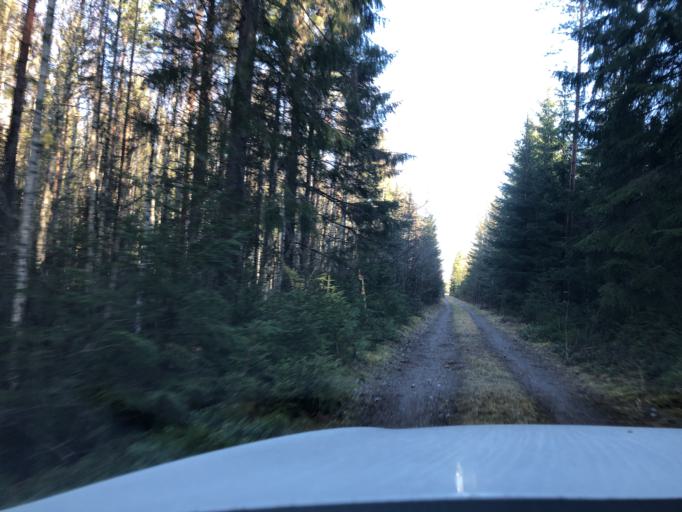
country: SE
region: Gaevleborg
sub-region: Gavle Kommun
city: Hedesunda
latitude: 60.2997
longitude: 16.9000
